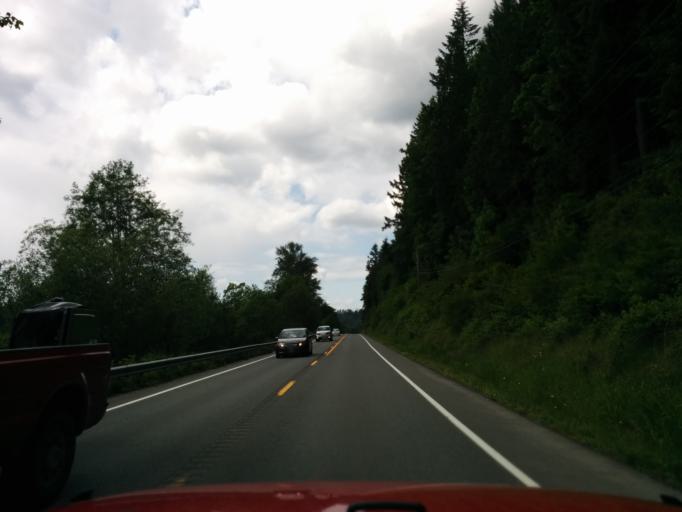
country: US
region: Washington
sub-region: King County
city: Ames Lake
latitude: 47.5847
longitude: -121.9467
